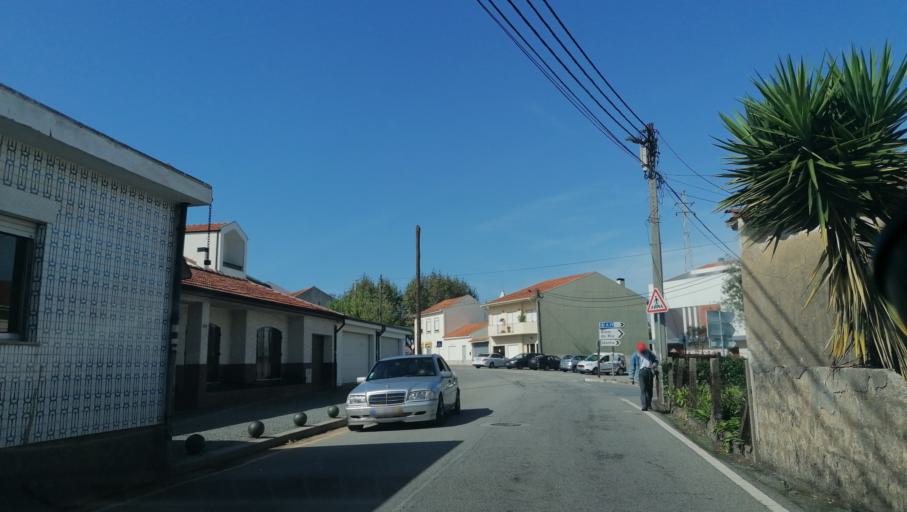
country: PT
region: Aveiro
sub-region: Espinho
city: Silvalde
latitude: 41.0053
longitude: -8.6239
